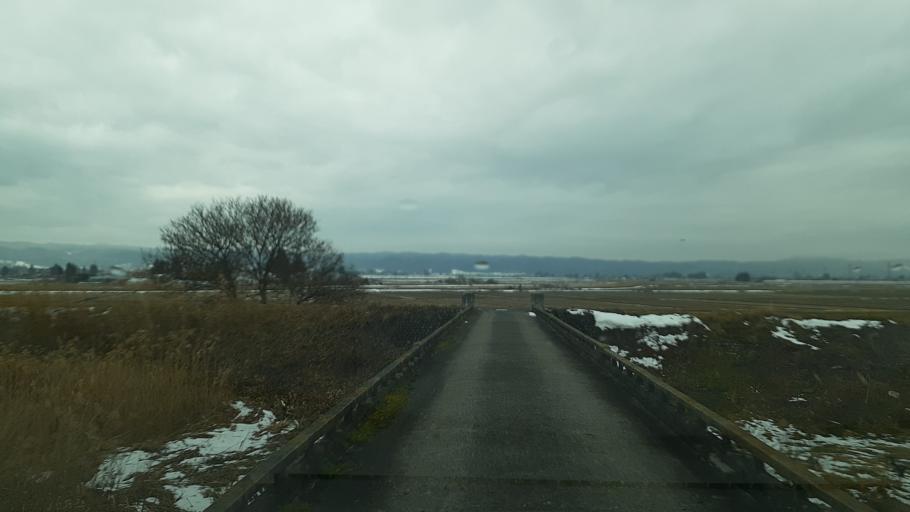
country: JP
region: Fukushima
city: Kitakata
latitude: 37.5367
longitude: 139.8474
